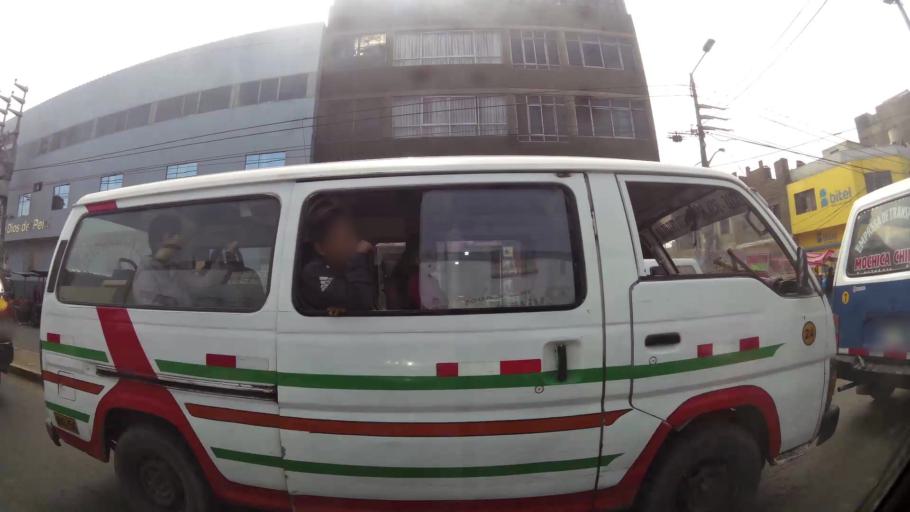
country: PE
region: La Libertad
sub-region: Provincia de Trujillo
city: Trujillo
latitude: -8.1130
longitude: -79.0200
